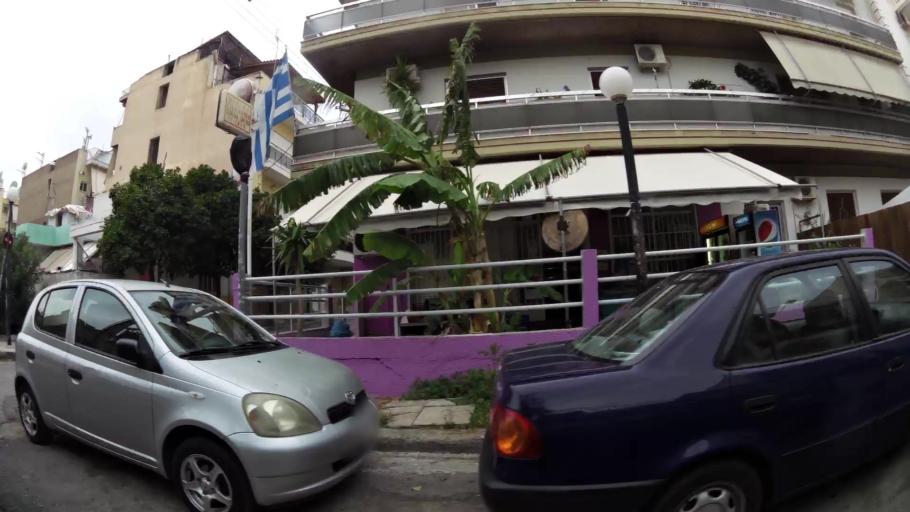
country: GR
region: Attica
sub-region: Nomos Piraios
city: Nikaia
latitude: 37.9620
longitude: 23.6538
